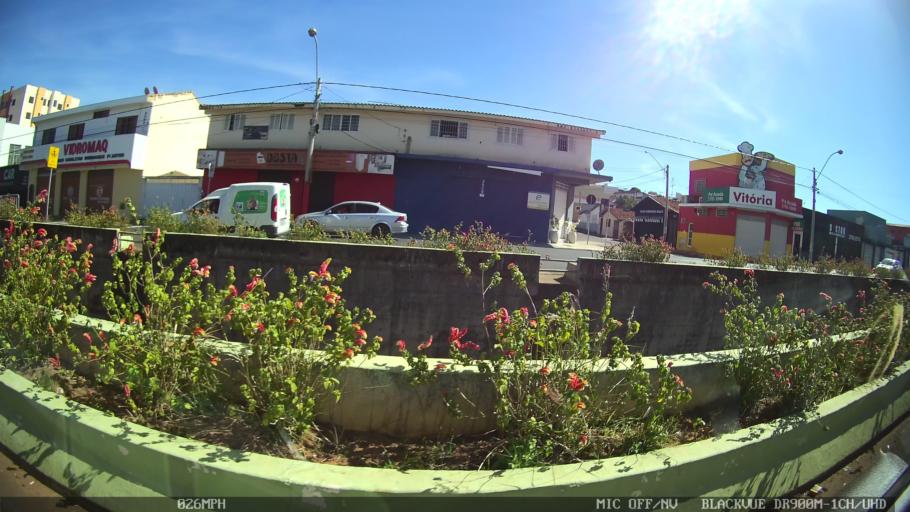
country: BR
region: Sao Paulo
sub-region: Franca
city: Franca
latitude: -20.5270
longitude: -47.4020
